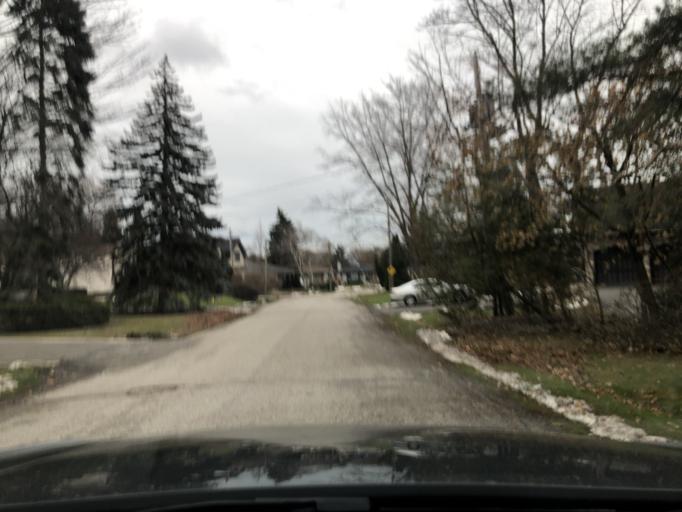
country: CA
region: Ontario
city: Etobicoke
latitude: 43.6912
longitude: -79.5247
